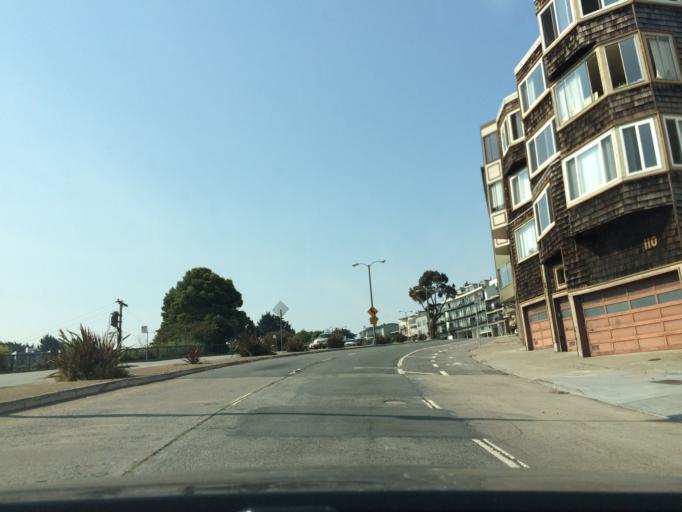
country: US
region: California
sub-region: San Francisco County
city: San Francisco
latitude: 37.7496
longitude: -122.4436
